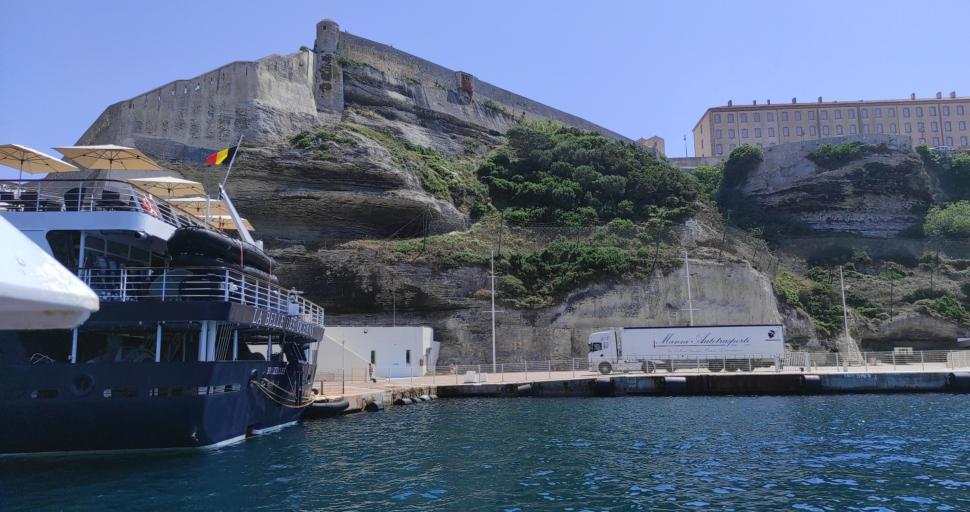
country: FR
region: Corsica
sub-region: Departement de la Corse-du-Sud
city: Bonifacio
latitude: 41.3891
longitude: 9.1562
